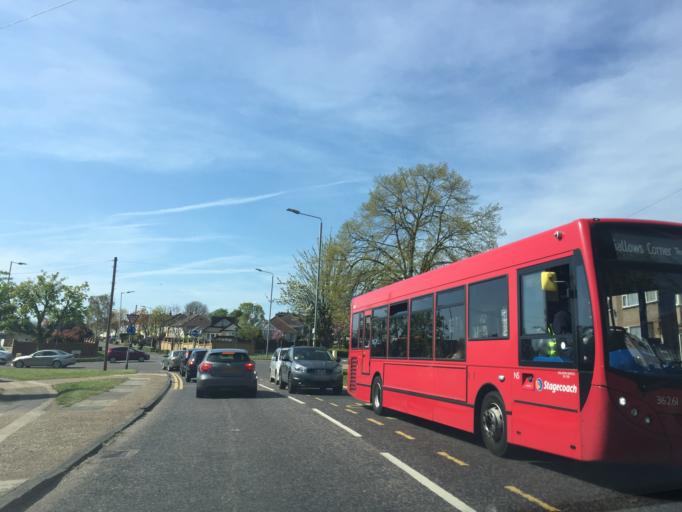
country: GB
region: England
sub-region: Greater London
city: Collier Row
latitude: 51.5971
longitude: 0.1750
